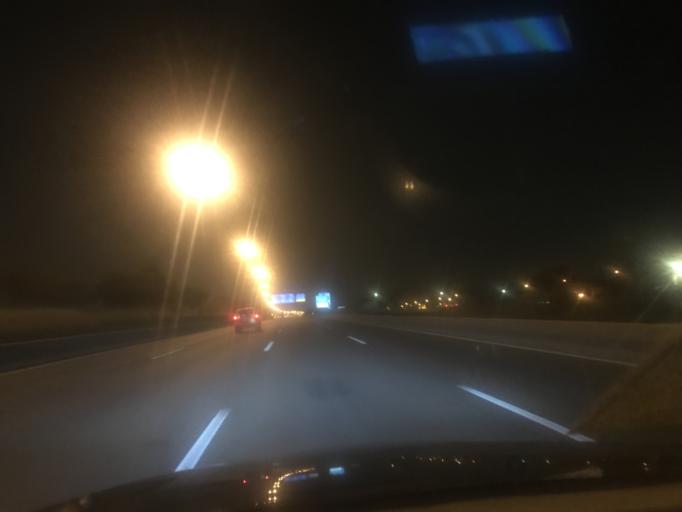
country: SA
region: Ar Riyad
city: Riyadh
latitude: 24.7637
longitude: 46.5774
